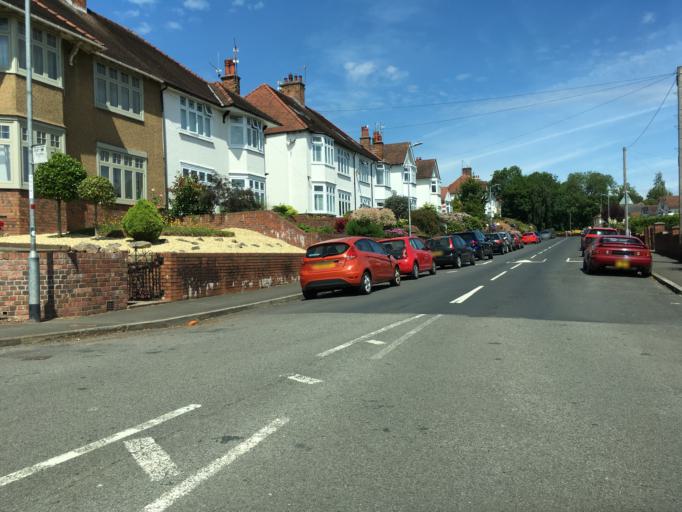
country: GB
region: Wales
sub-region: Newport
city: Newport
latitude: 51.5909
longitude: -3.0076
